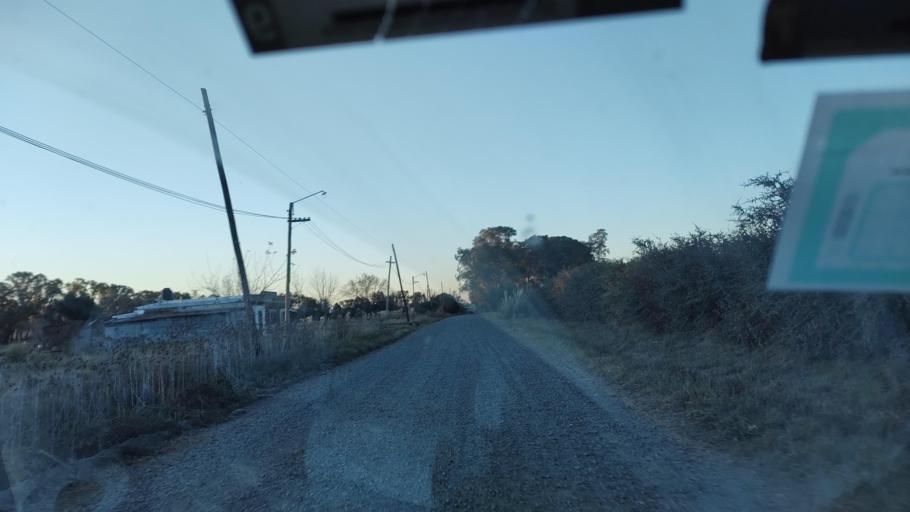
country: AR
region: Buenos Aires
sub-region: Partido de La Plata
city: La Plata
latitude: -34.9102
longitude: -58.0540
